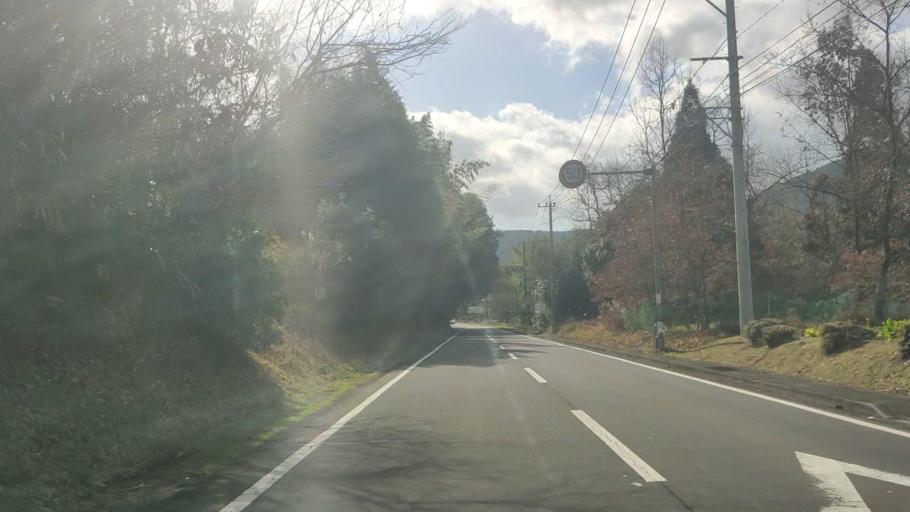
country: JP
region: Kagoshima
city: Okuchi-shinohara
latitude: 31.9874
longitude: 130.7437
